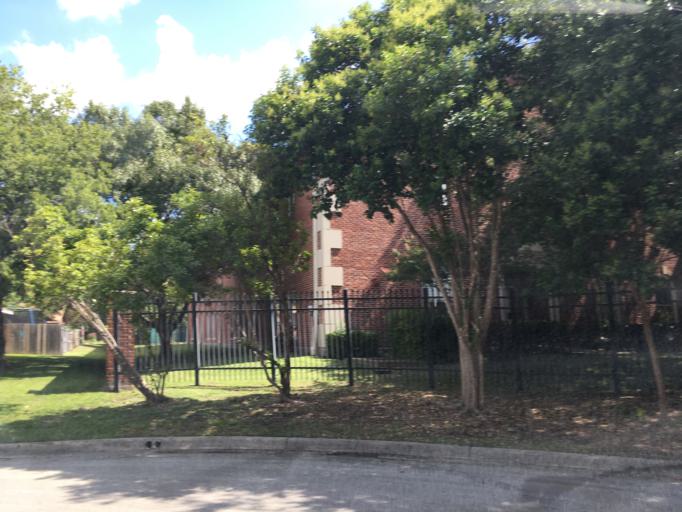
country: US
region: Texas
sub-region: Dallas County
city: Farmers Branch
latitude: 32.9248
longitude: -96.8750
